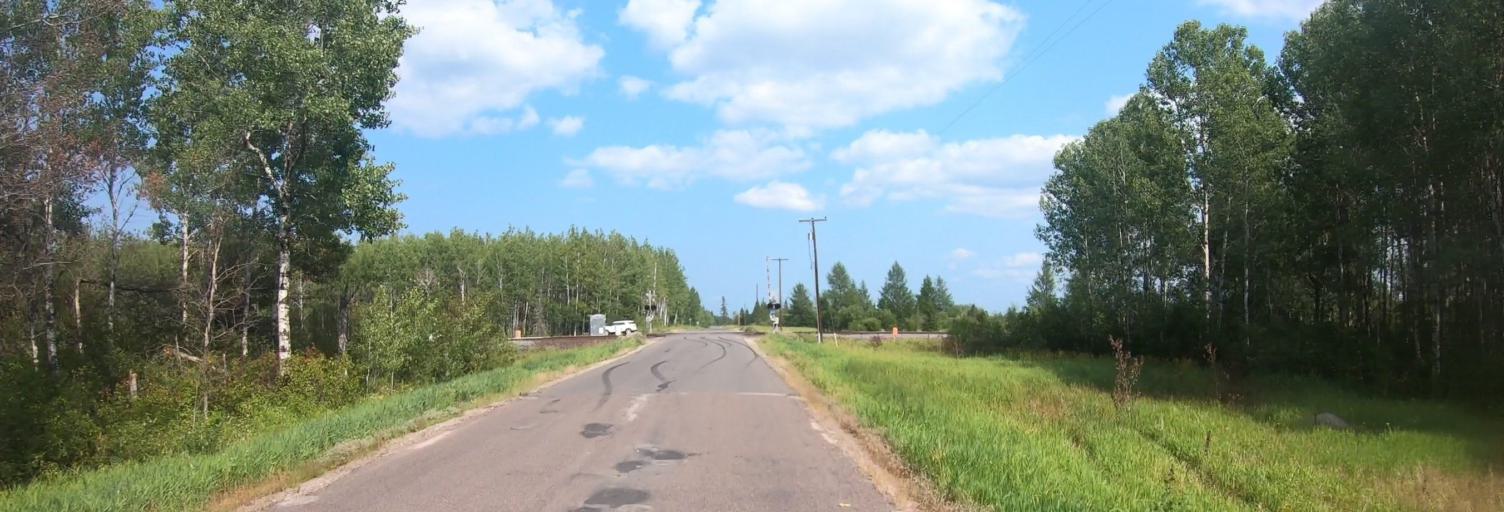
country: US
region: Minnesota
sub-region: Saint Louis County
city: Mountain Iron
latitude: 47.8920
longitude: -92.7145
